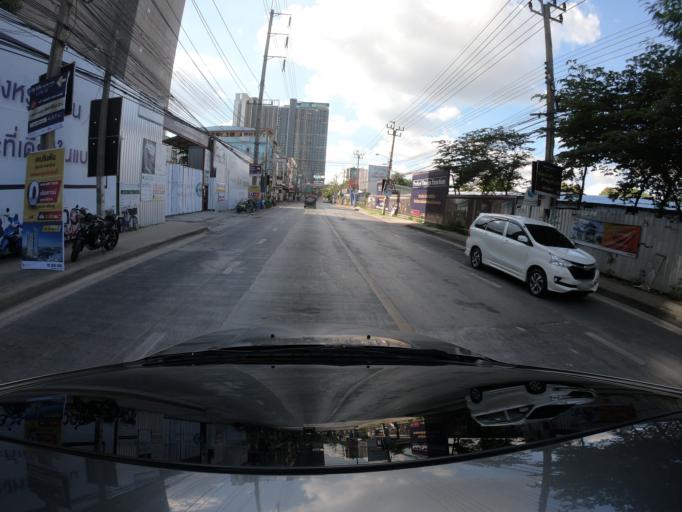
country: TH
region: Bangkok
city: Bang Na
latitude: 13.6578
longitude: 100.6033
